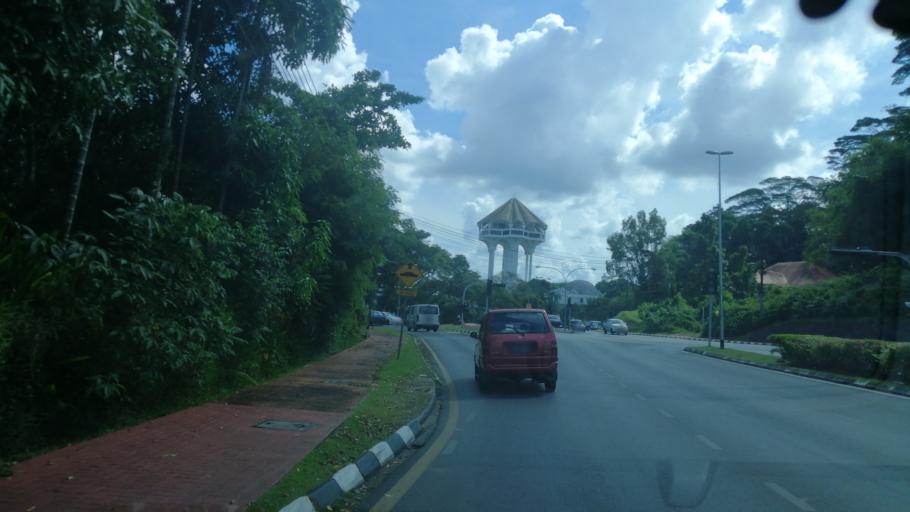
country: MY
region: Sarawak
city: Kuching
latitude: 1.5480
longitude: 110.3482
